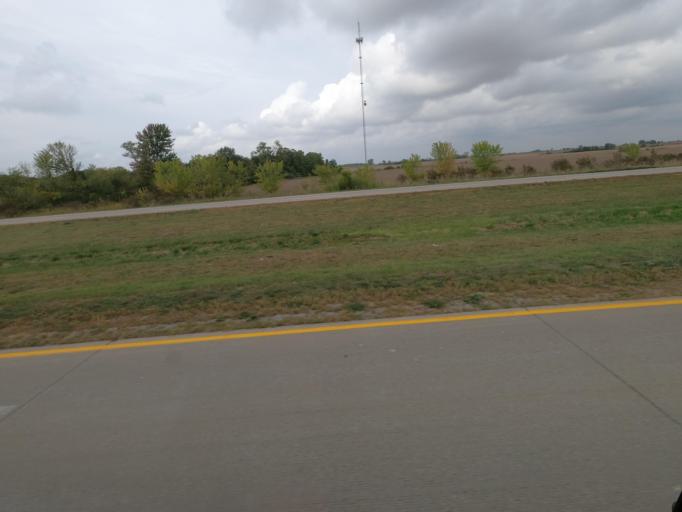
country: US
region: Iowa
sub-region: Wapello County
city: Ottumwa
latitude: 40.9987
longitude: -92.3248
